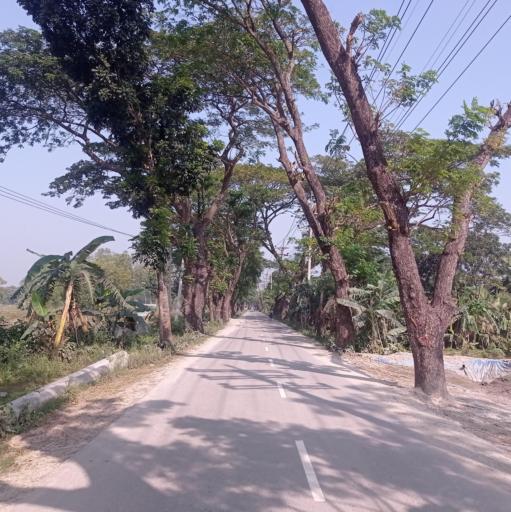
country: BD
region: Dhaka
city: Narsingdi
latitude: 24.0543
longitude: 90.6838
